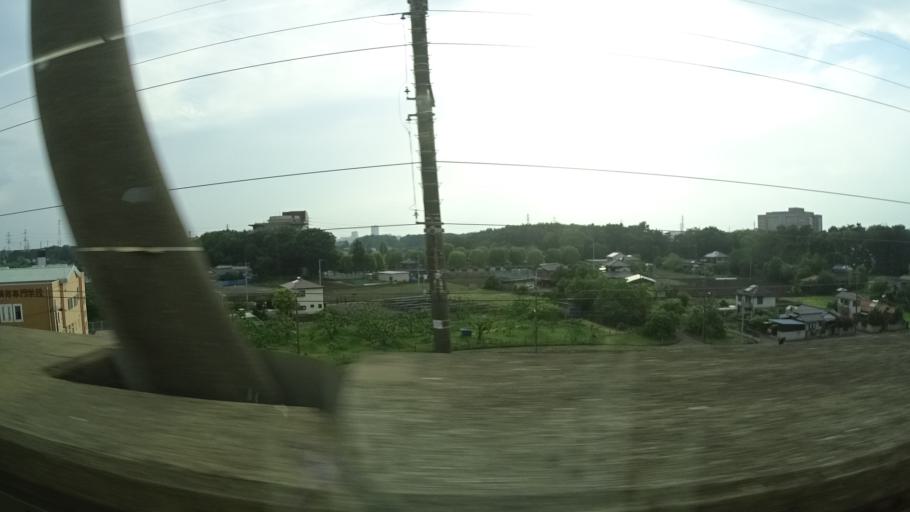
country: JP
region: Saitama
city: Ageoshimo
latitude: 35.9817
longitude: 139.6247
